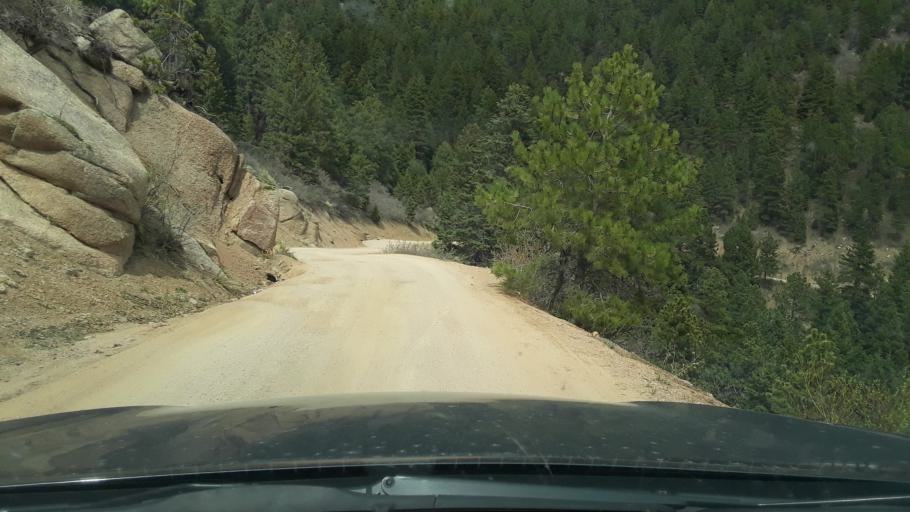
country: US
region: Colorado
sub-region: El Paso County
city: Palmer Lake
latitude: 39.0689
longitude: -104.9311
